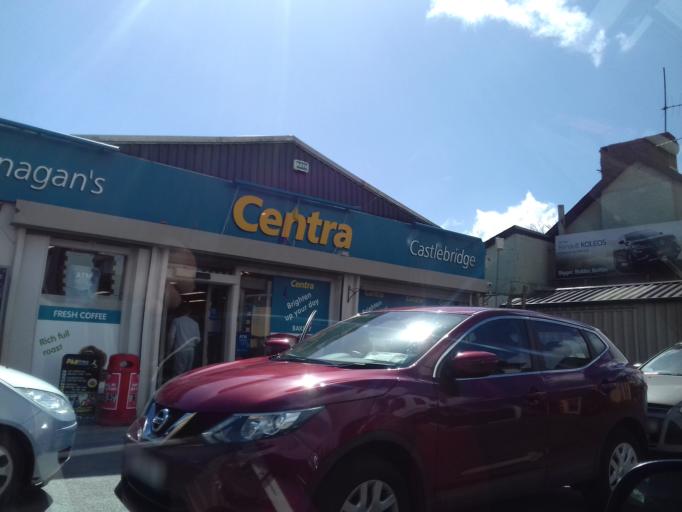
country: IE
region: Leinster
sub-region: Loch Garman
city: Castlebridge
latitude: 52.3817
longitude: -6.4503
